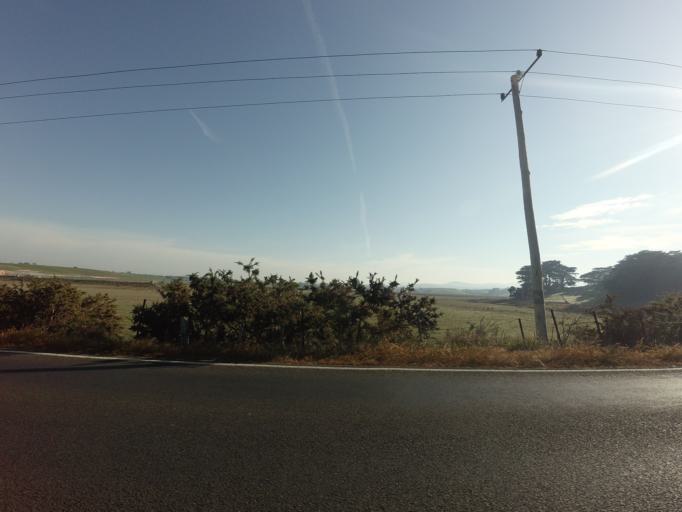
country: AU
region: Tasmania
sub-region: Launceston
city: Summerhill
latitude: -41.5277
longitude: 147.0211
